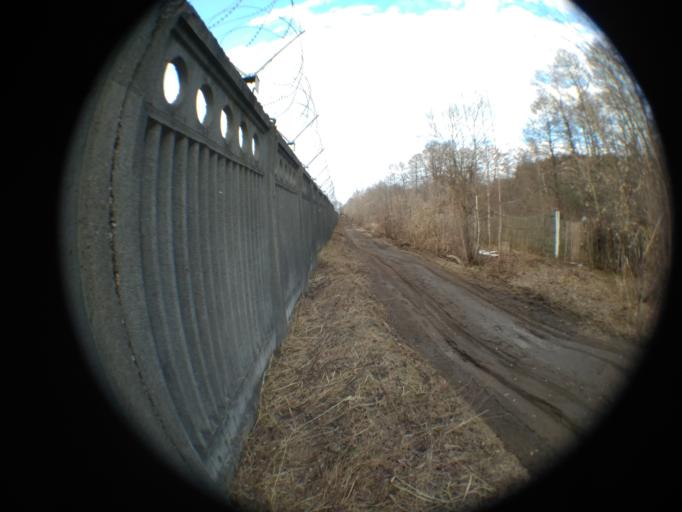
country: RU
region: Moskovskaya
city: Kratovo
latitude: 55.5696
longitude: 38.1698
